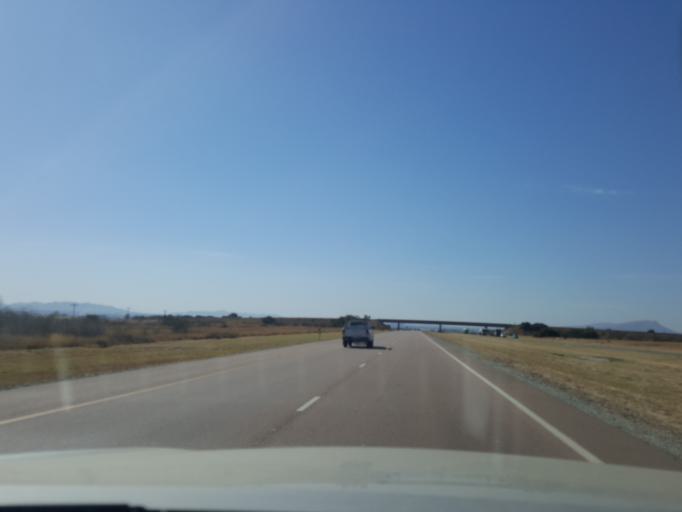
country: ZA
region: North-West
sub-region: Bojanala Platinum District Municipality
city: Brits
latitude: -25.6881
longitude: 27.7546
